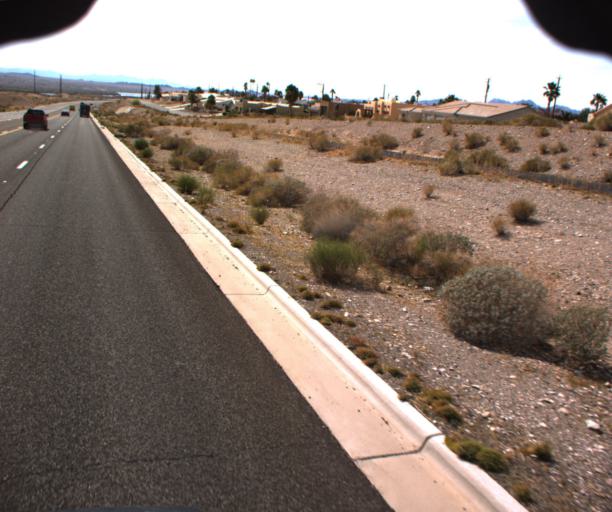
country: US
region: Arizona
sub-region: Mohave County
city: Lake Havasu City
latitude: 34.4534
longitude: -114.3048
